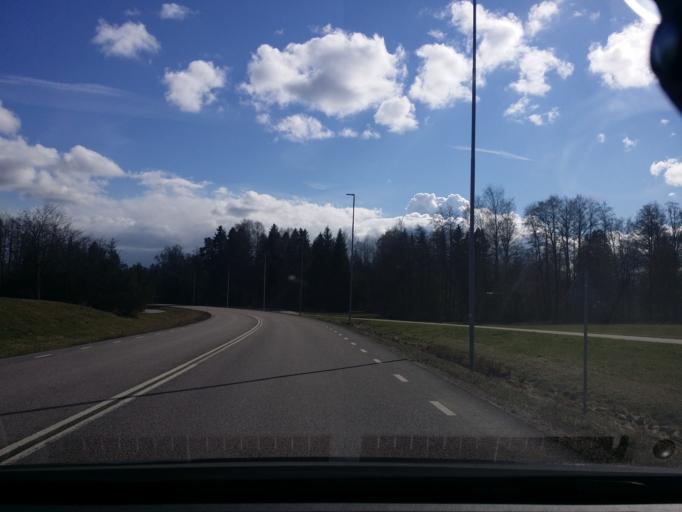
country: SE
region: Vaestmanland
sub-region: Sala Kommun
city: Sala
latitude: 59.9308
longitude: 16.5726
